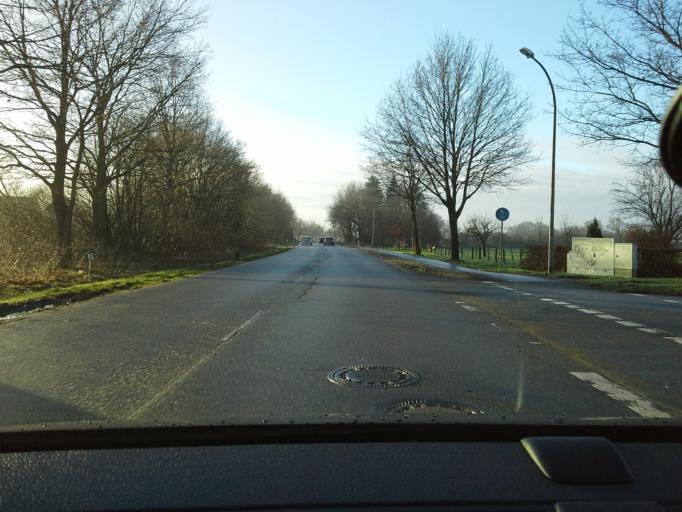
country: DE
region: Schleswig-Holstein
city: Borstel-Hohenraden
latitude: 53.6947
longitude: 9.8210
